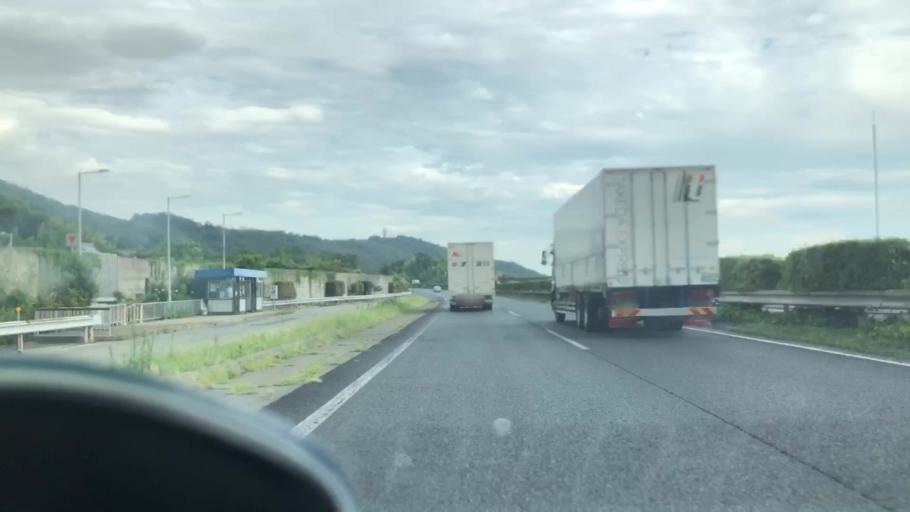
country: JP
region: Hyogo
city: Ono
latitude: 34.9354
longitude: 134.8365
